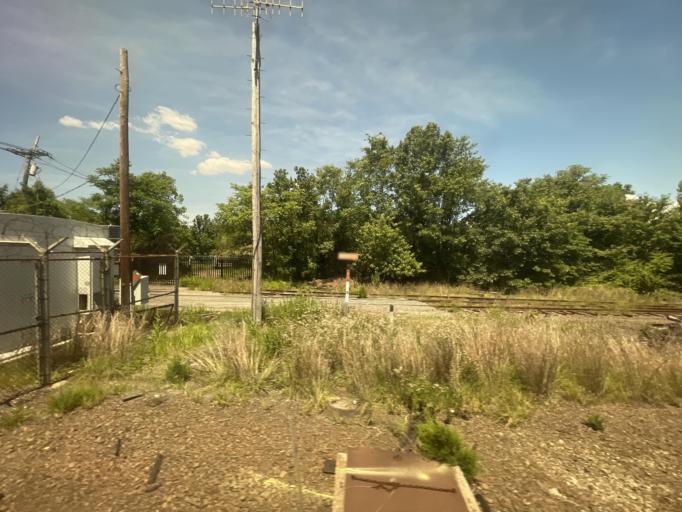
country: US
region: New Jersey
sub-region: Middlesex County
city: Edison
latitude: 40.5197
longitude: -74.4104
